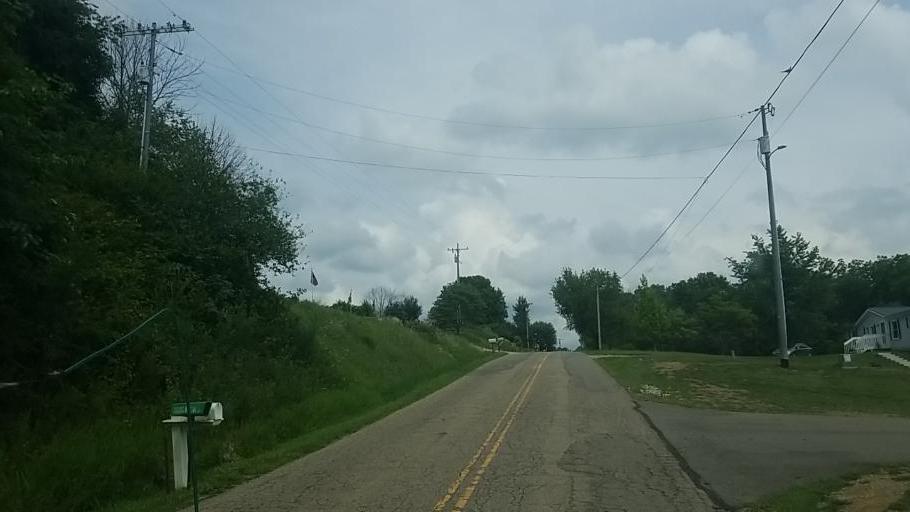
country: US
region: Ohio
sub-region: Knox County
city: Mount Vernon
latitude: 40.3211
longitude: -82.4682
